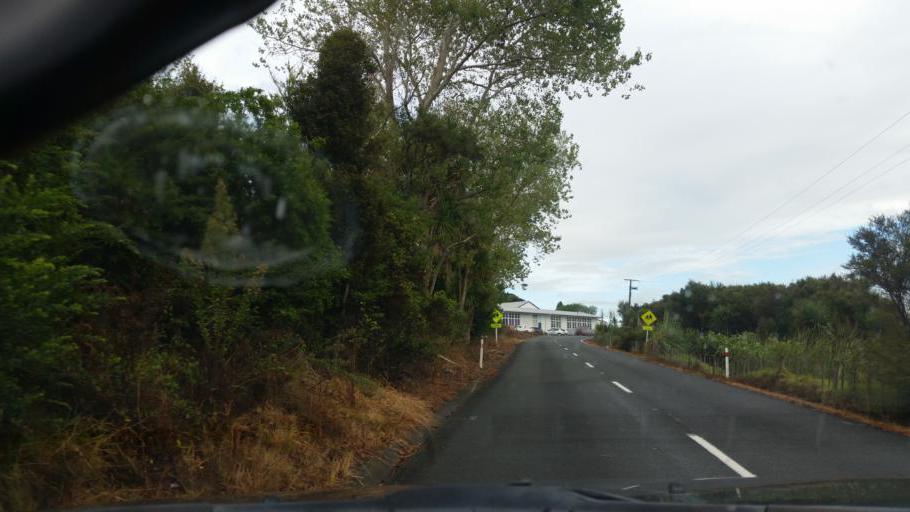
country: NZ
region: Auckland
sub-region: Auckland
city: Wellsford
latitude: -36.1180
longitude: 174.3665
